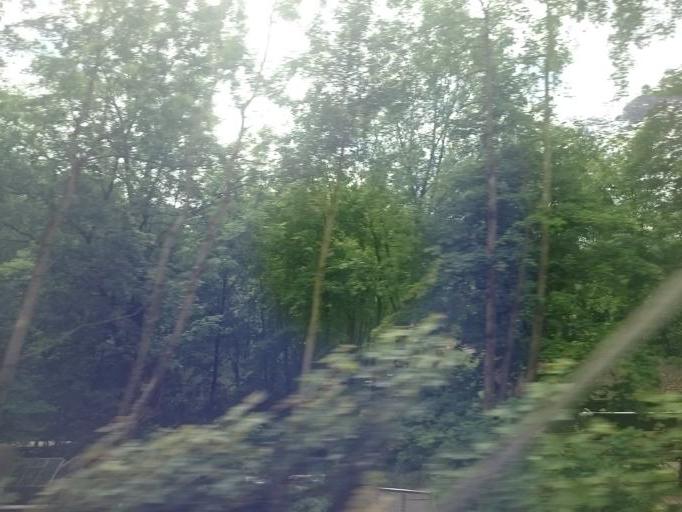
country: DE
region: Bavaria
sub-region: Upper Bavaria
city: Munich
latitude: 48.1176
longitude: 11.5629
